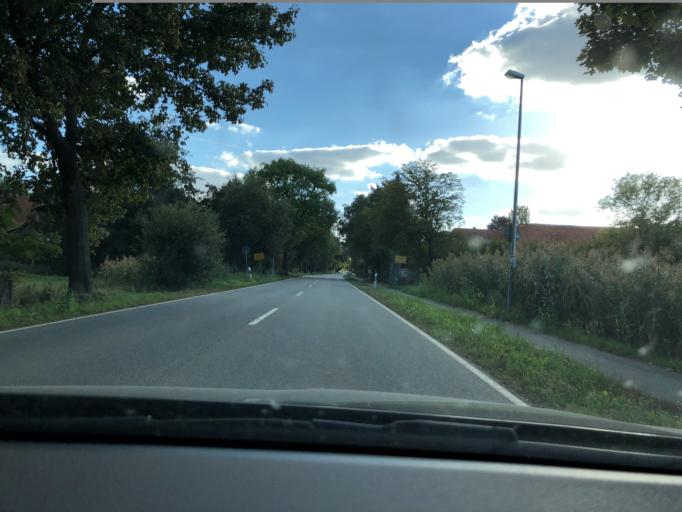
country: DE
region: Lower Saxony
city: Stuhr
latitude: 53.0330
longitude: 8.7583
